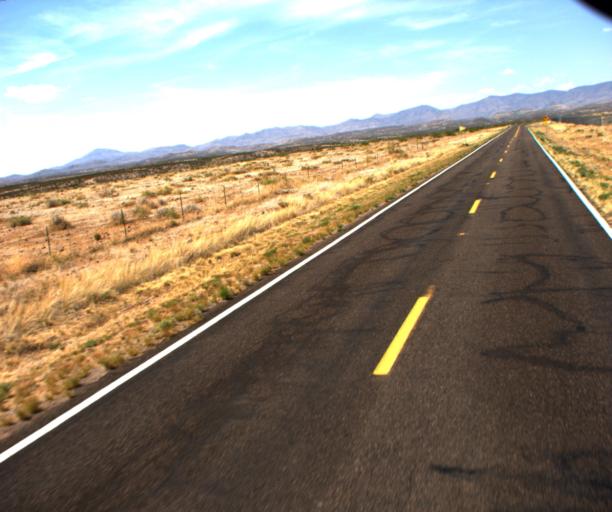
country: US
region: Arizona
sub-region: Greenlee County
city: Clifton
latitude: 32.9550
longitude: -109.2218
